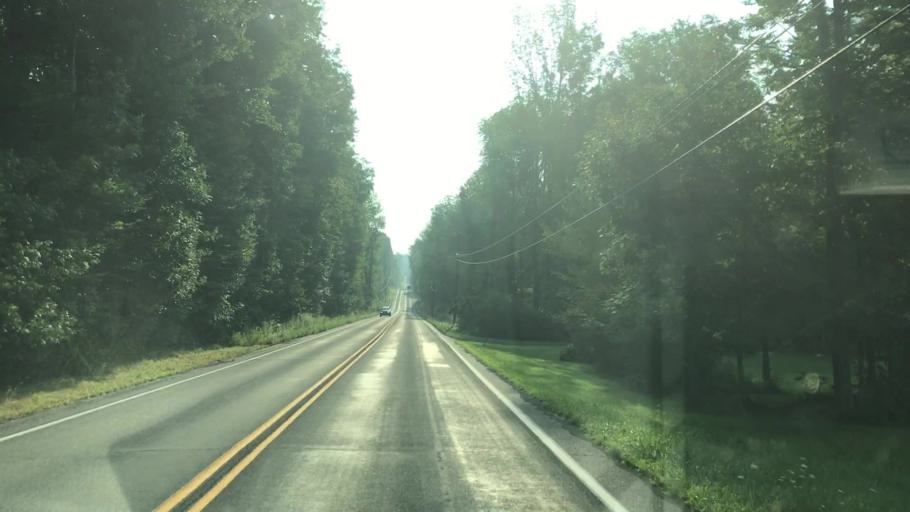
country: US
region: Pennsylvania
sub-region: Lackawanna County
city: Dalton
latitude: 41.5990
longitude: -75.7008
